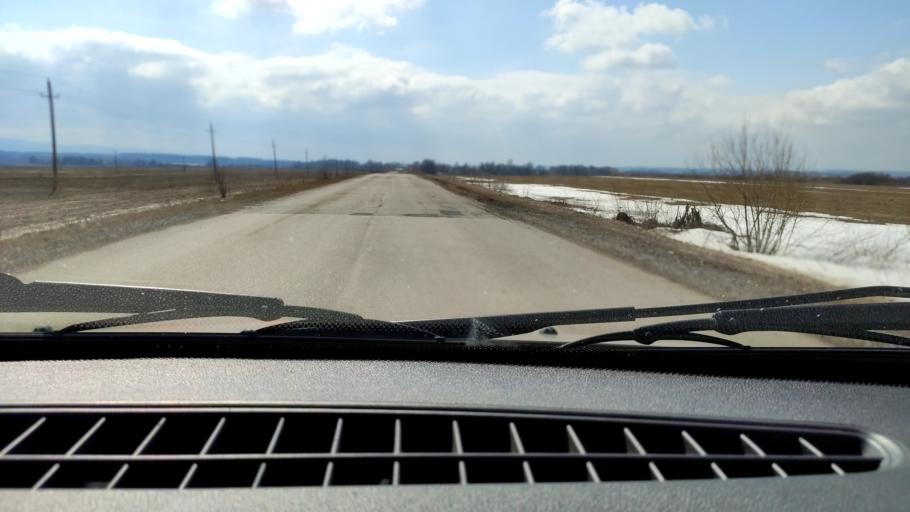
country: RU
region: Bashkortostan
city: Kudeyevskiy
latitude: 54.8410
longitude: 56.7949
